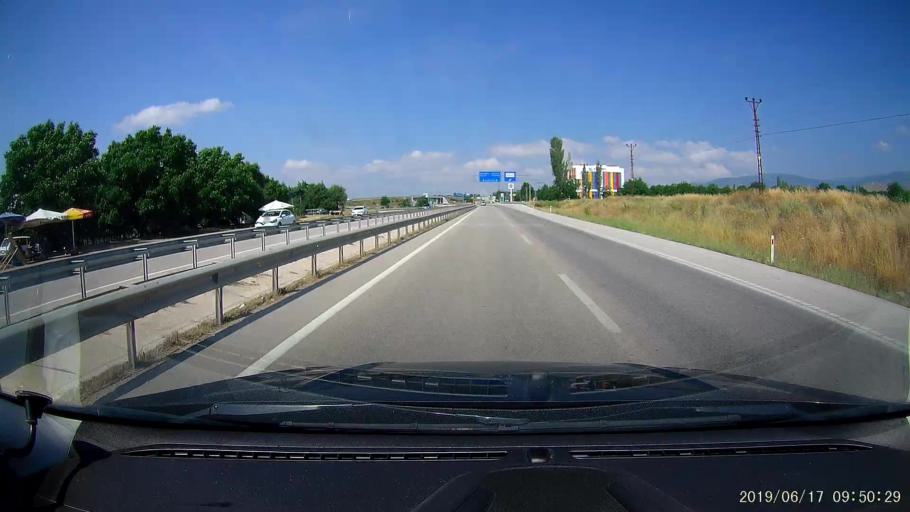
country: TR
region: Amasya
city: Merzifon
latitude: 40.8708
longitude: 35.5058
